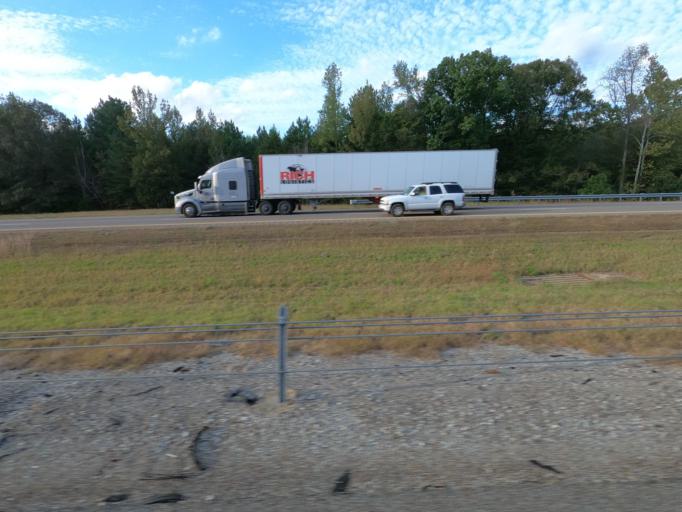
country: US
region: Tennessee
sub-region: Henderson County
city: Lexington
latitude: 35.8136
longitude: -88.2864
